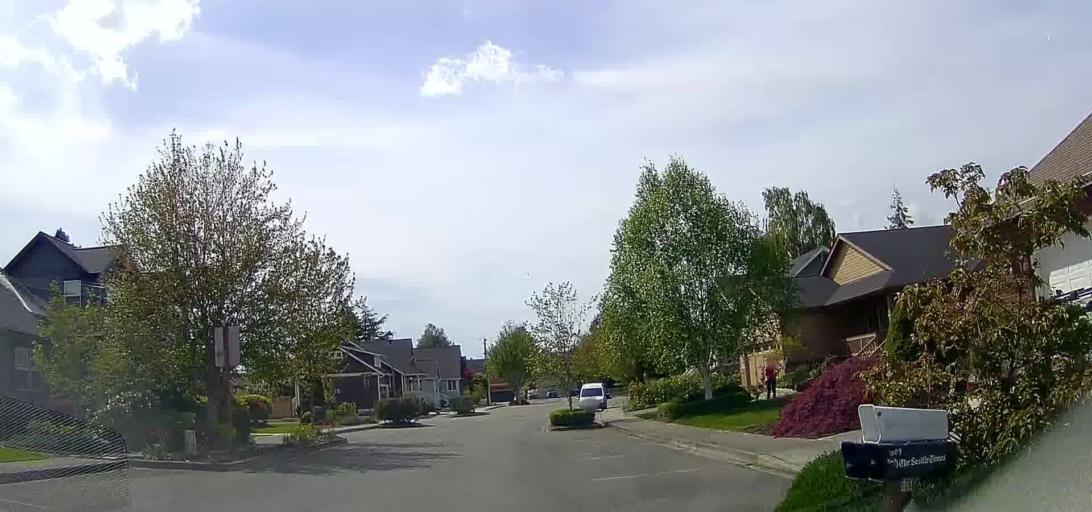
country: US
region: Washington
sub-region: Skagit County
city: Mount Vernon
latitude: 48.3933
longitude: -122.4890
